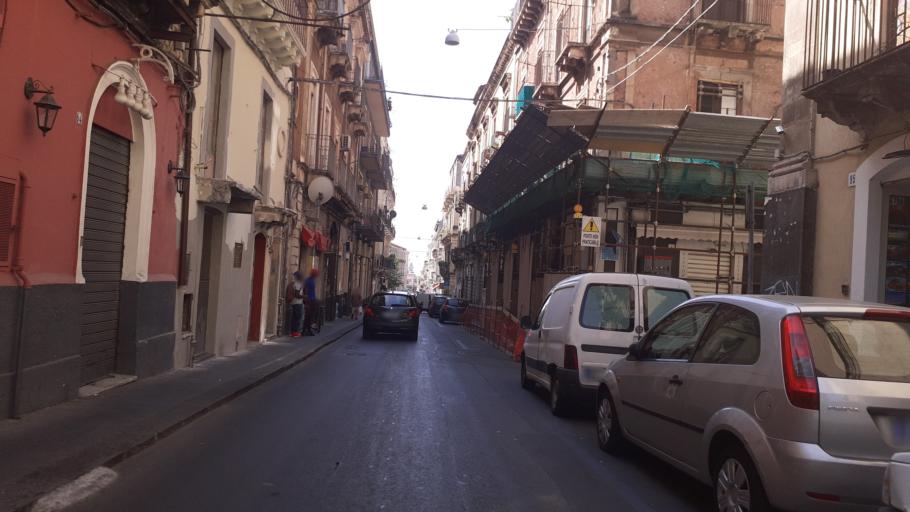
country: IT
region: Sicily
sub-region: Catania
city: Catania
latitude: 37.5064
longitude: 15.0931
